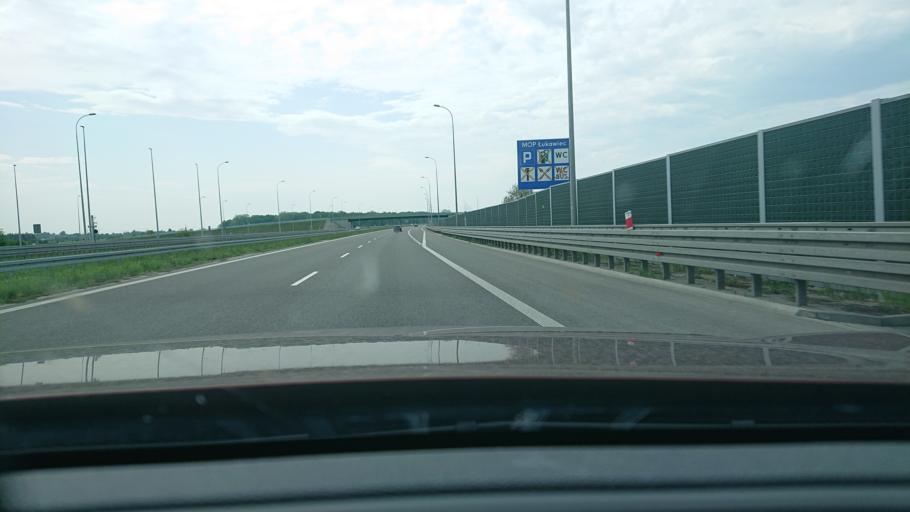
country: PL
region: Subcarpathian Voivodeship
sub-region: Powiat lancucki
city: Czarna
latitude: 50.0908
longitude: 22.1620
